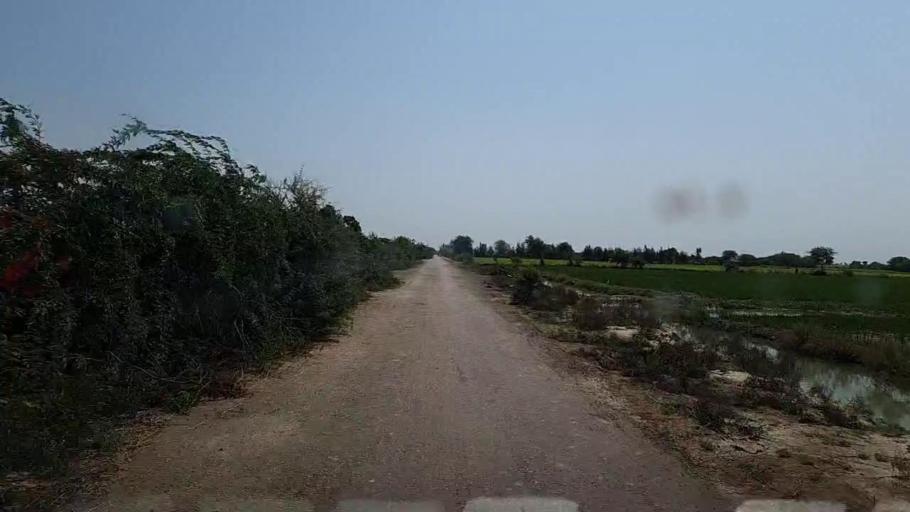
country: PK
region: Sindh
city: Mirpur Batoro
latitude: 24.6181
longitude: 68.4522
